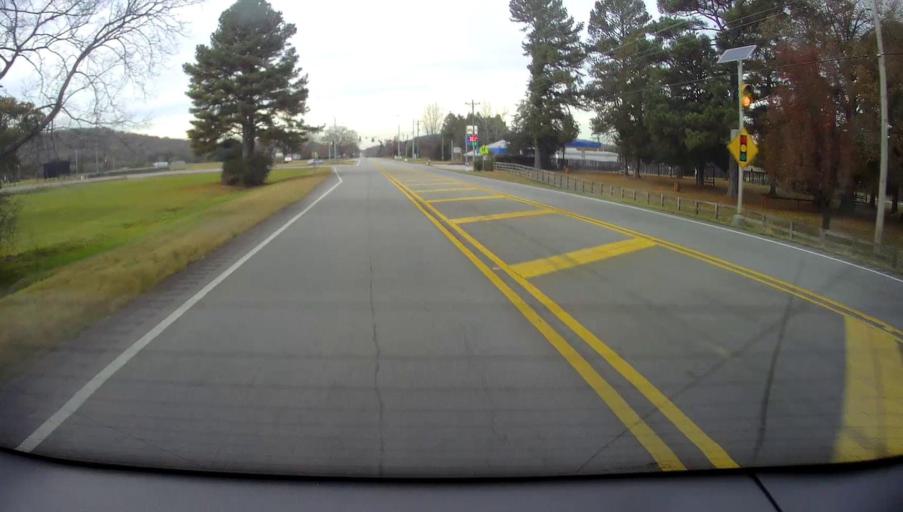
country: US
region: Alabama
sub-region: Morgan County
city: Falkville
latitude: 34.4150
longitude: -86.7029
